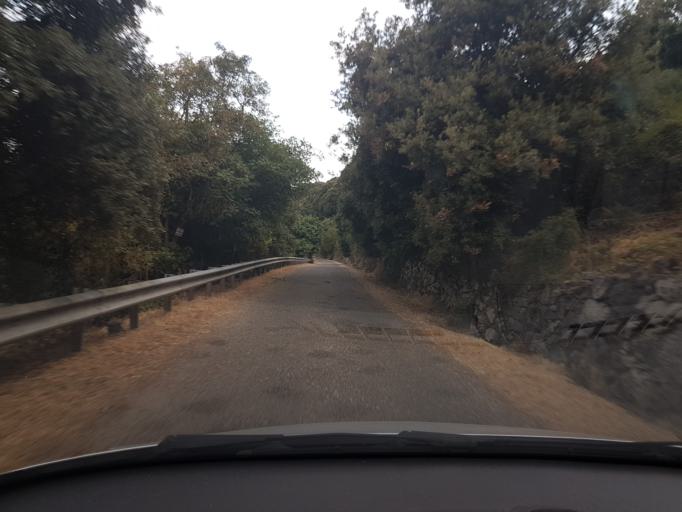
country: IT
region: Sardinia
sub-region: Provincia di Oristano
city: Seneghe
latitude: 40.1116
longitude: 8.6069
